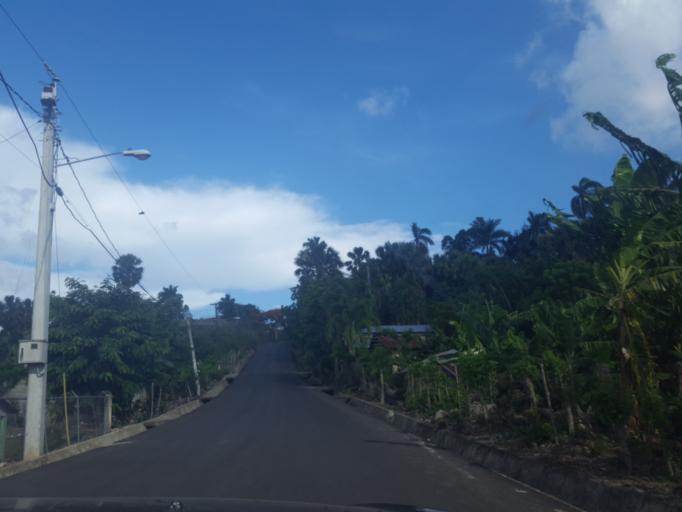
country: DO
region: La Vega
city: Rio Verde Arriba
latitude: 19.3552
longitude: -70.6309
